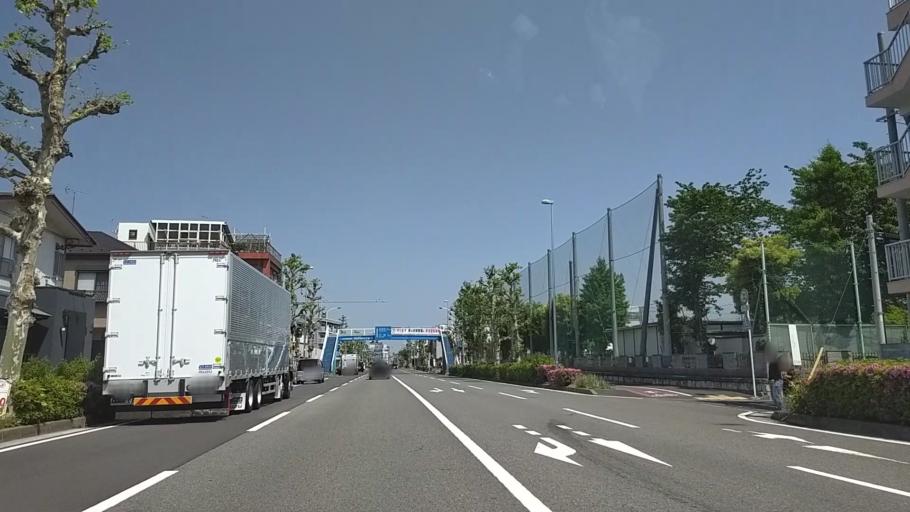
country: JP
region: Kanagawa
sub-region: Kawasaki-shi
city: Kawasaki
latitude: 35.5114
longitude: 139.6915
